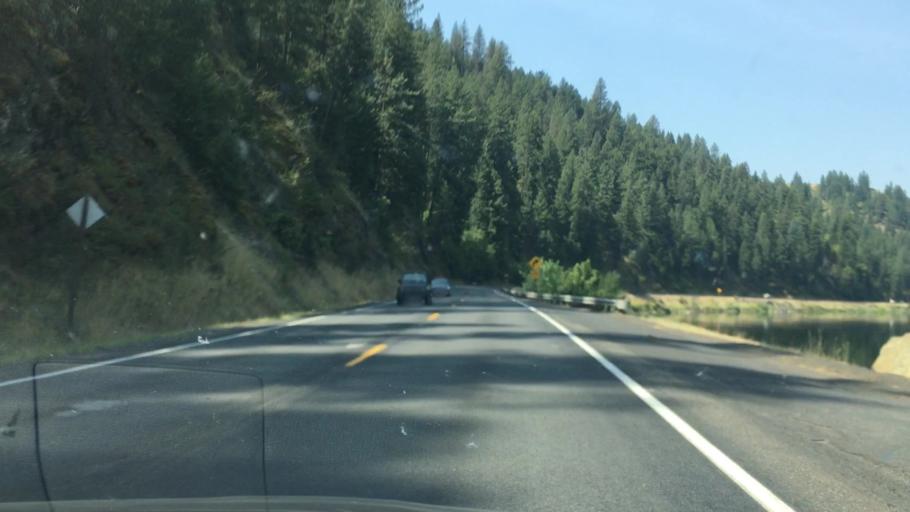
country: US
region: Idaho
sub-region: Clearwater County
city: Orofino
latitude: 46.4993
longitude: -116.3716
